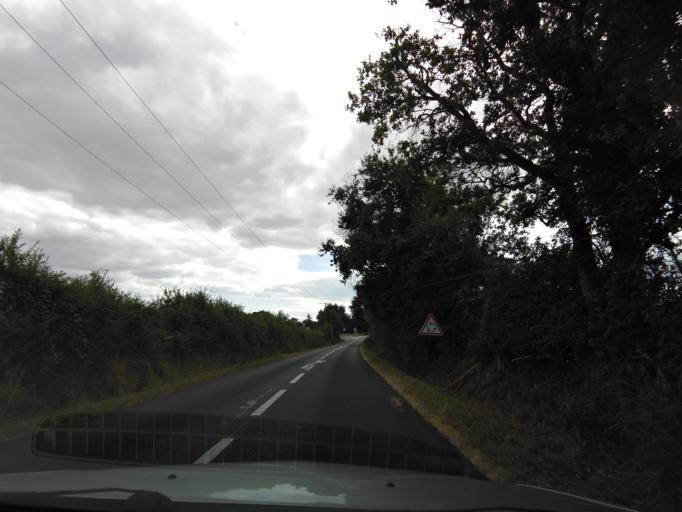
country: FR
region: Pays de la Loire
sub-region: Departement de la Vendee
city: Avrille
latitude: 46.4635
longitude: -1.4538
